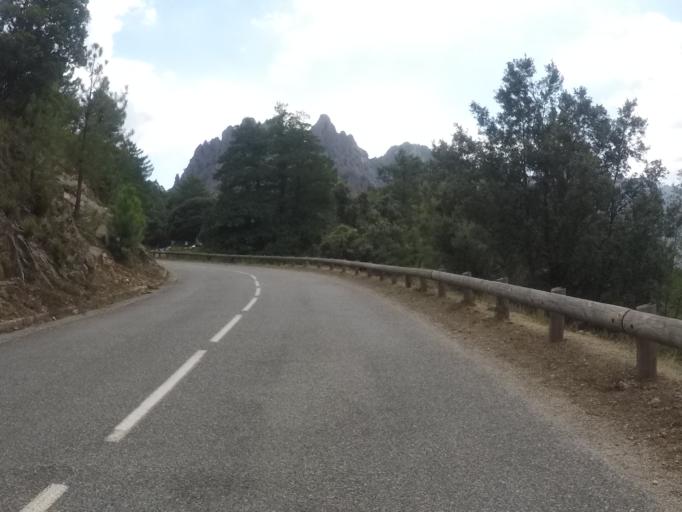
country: FR
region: Corsica
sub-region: Departement de la Corse-du-Sud
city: Sari-Solenzara
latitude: 41.8276
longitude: 9.2716
